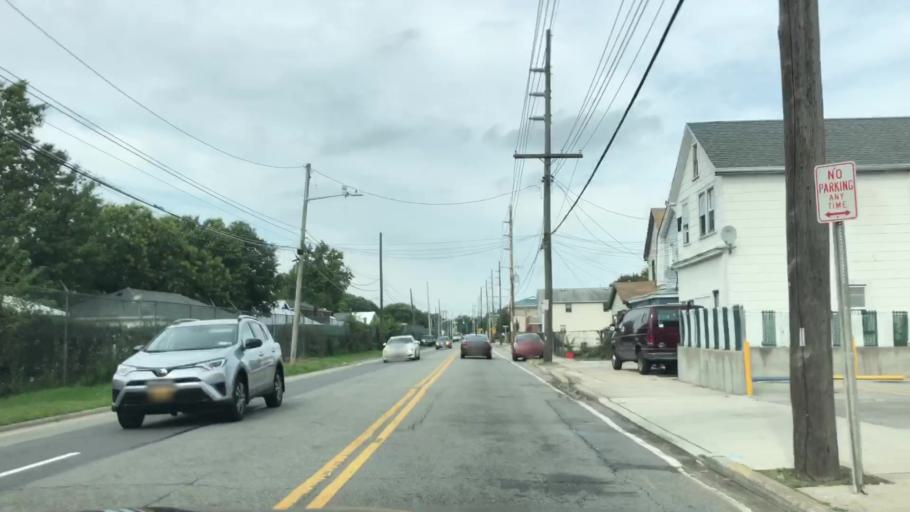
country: US
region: New York
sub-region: Nassau County
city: South Floral Park
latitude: 40.7107
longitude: -73.7089
